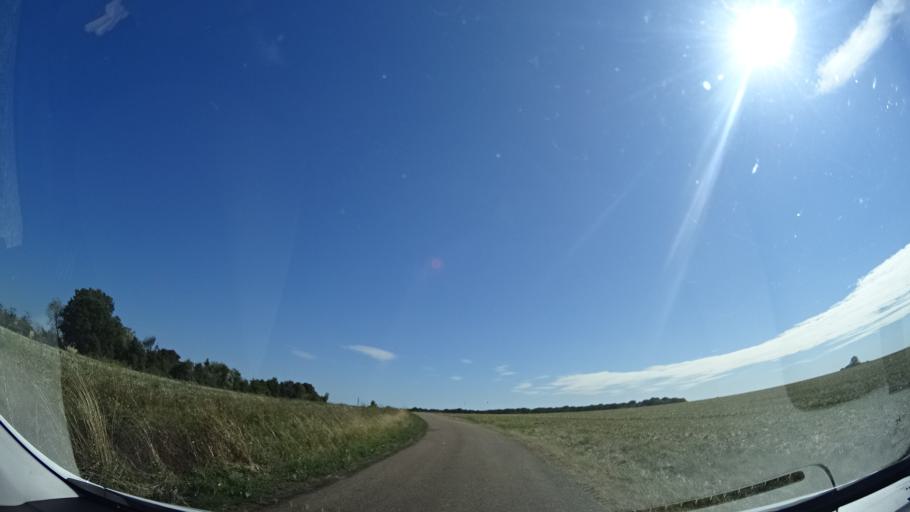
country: FR
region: Centre
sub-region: Departement du Loiret
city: Trigueres
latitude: 47.9566
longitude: 2.9676
